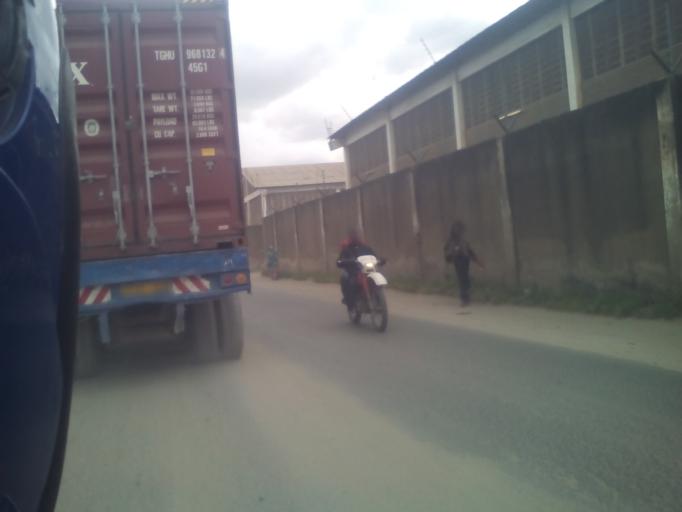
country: TZ
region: Dar es Salaam
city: Dar es Salaam
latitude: -6.8543
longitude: 39.2309
